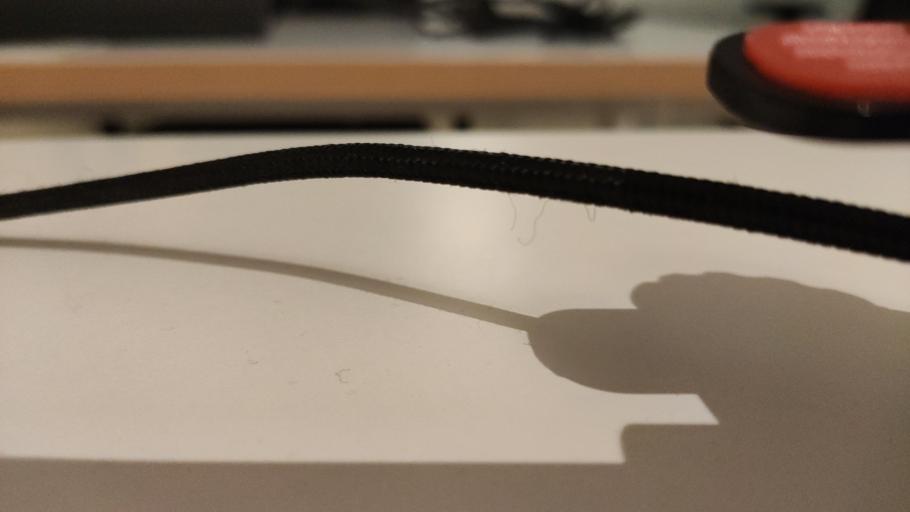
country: RU
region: Moskovskaya
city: Shaburnovo
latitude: 56.4382
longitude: 37.9131
